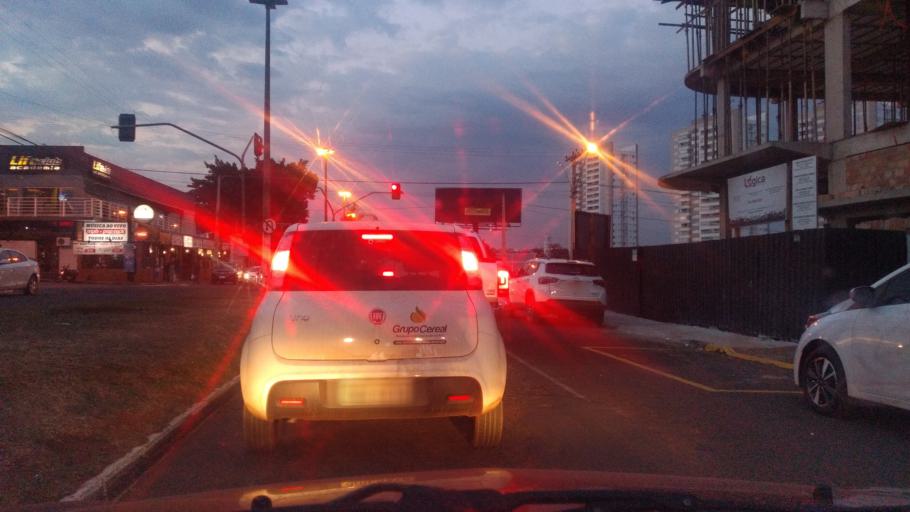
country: BR
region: Goias
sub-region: Santa Helena De Goias
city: Santa Helena de Goias
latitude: -17.7919
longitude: -50.9437
